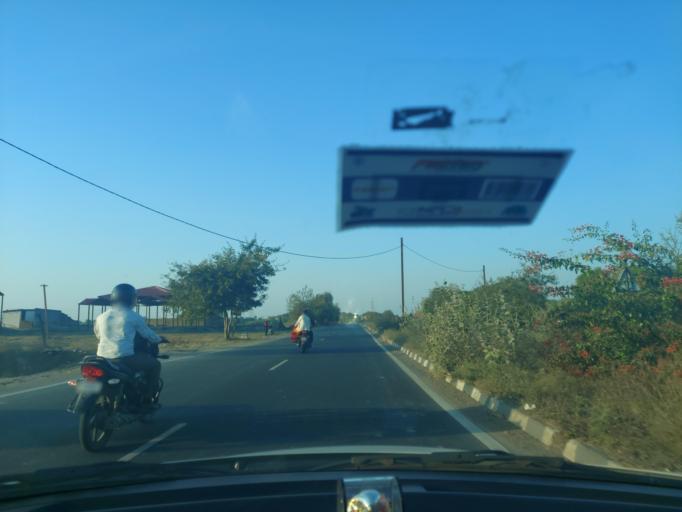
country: IN
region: Madhya Pradesh
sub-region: Indore
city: Sanwer
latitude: 23.0513
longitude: 75.8260
